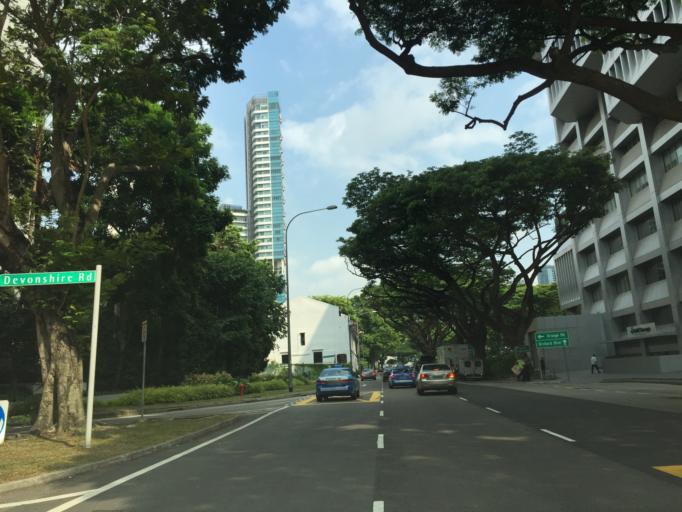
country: SG
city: Singapore
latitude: 1.2997
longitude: 103.8376
